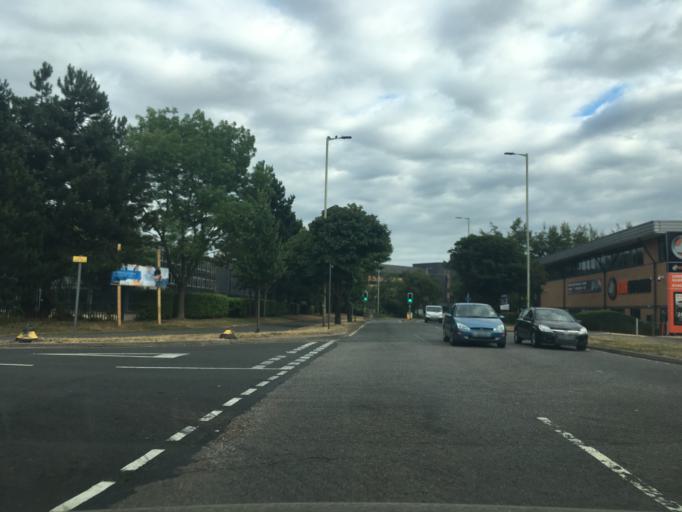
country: GB
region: England
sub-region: Hertfordshire
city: Hemel Hempstead
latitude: 51.7631
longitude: -0.4396
